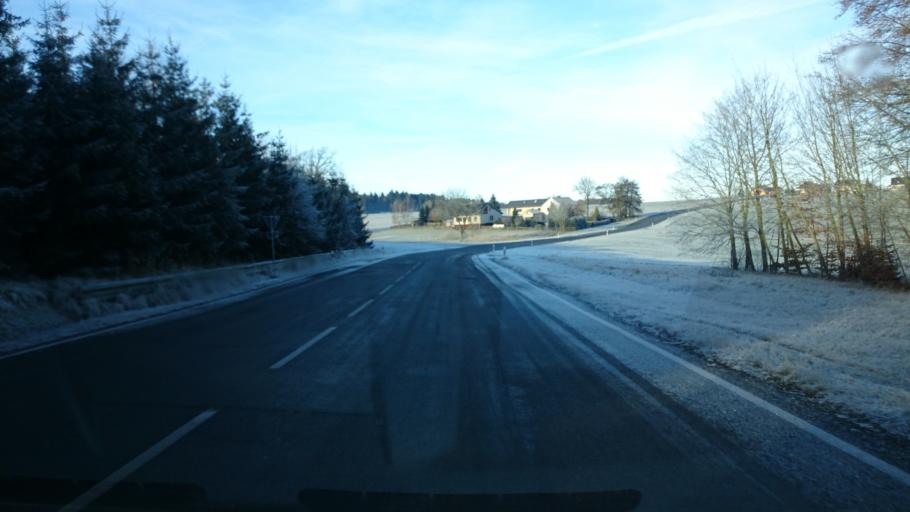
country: DE
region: Thuringia
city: Schleiz
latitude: 50.5526
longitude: 11.8338
